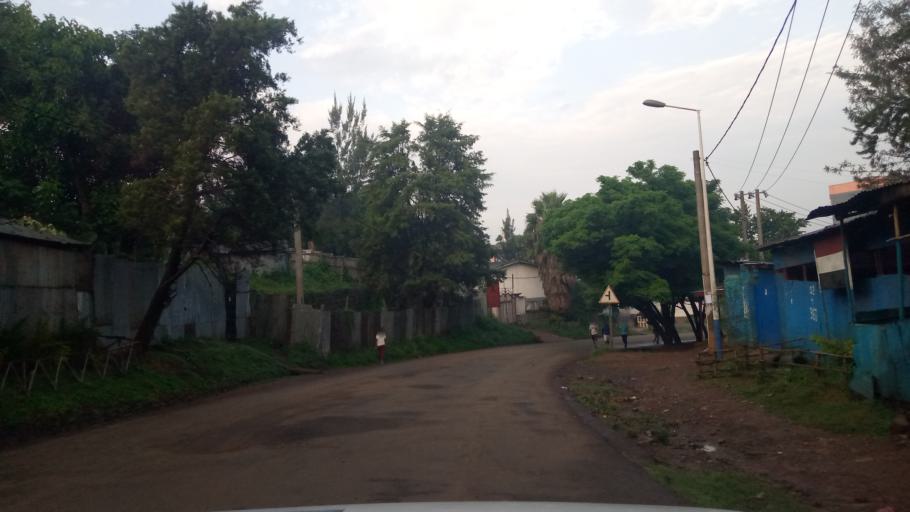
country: ET
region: Oromiya
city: Jima
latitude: 7.6757
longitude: 36.8387
